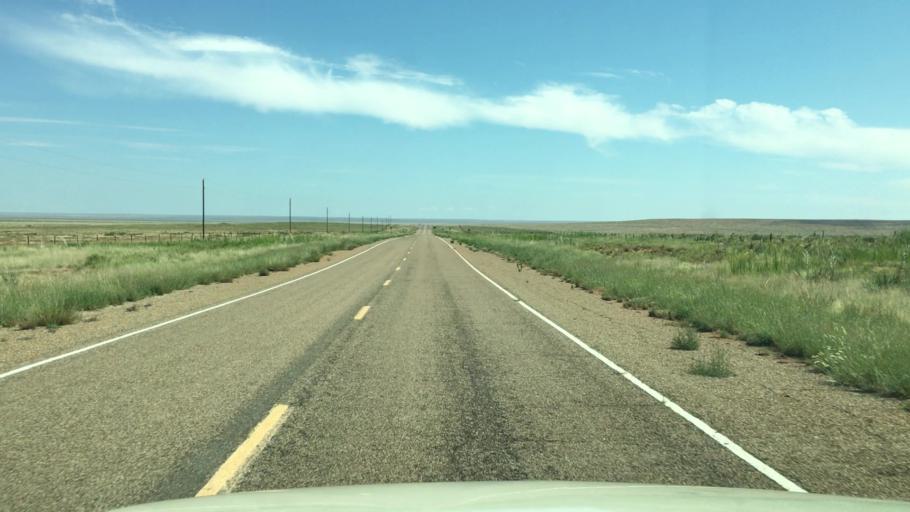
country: US
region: New Mexico
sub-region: De Baca County
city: Fort Sumner
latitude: 33.9936
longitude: -104.5691
